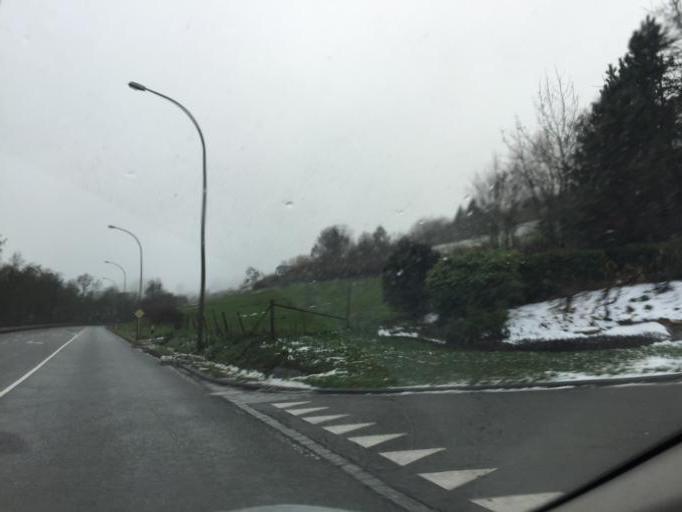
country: LU
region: Diekirch
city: Warken
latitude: 49.8502
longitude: 6.0724
